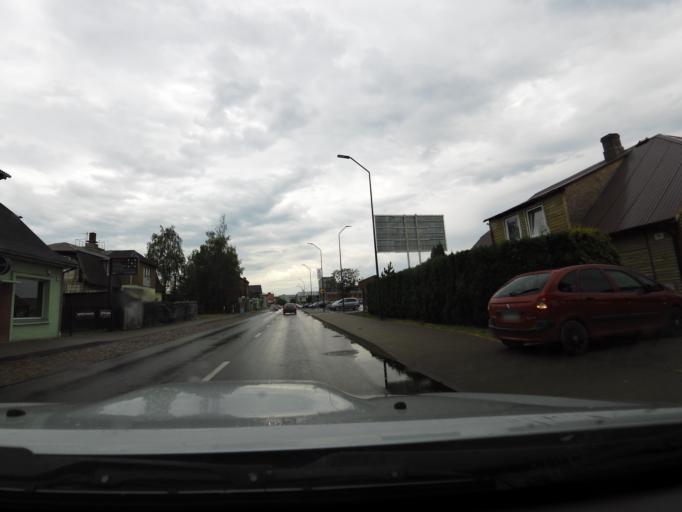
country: LT
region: Marijampoles apskritis
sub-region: Marijampole Municipality
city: Marijampole
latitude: 54.5559
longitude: 23.3577
